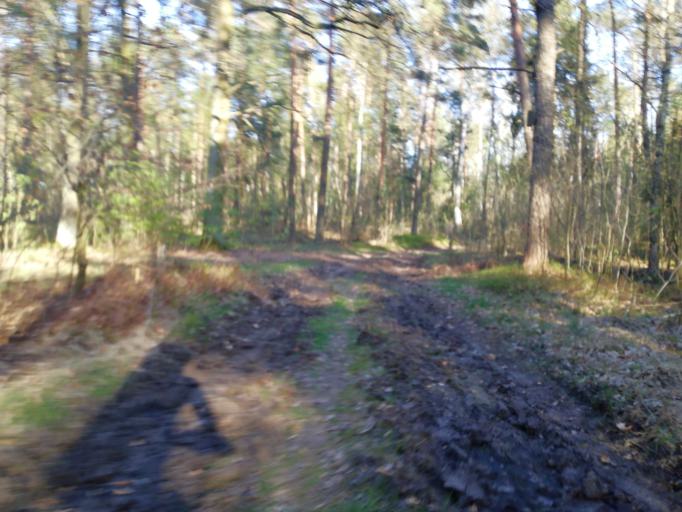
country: DE
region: Brandenburg
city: Calau
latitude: 51.7236
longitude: 13.9662
